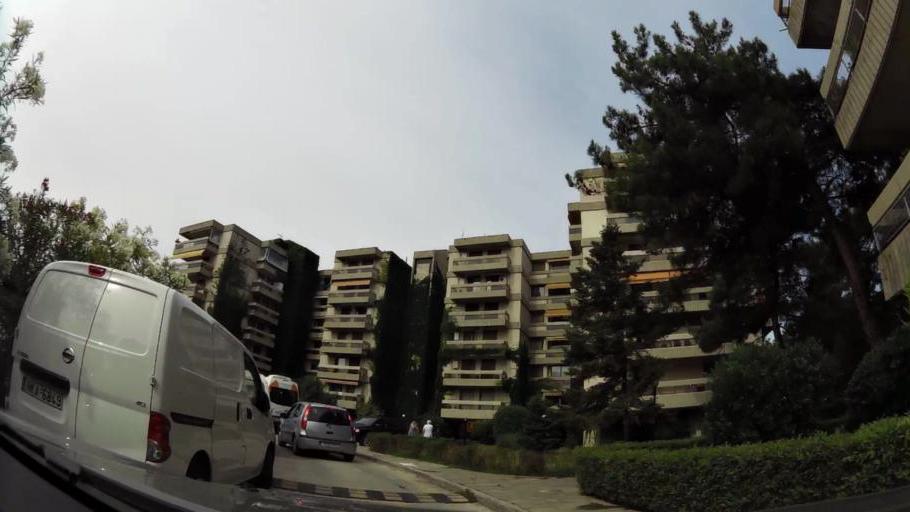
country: GR
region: Central Macedonia
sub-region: Nomos Thessalonikis
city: Pylaia
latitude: 40.5935
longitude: 23.0068
